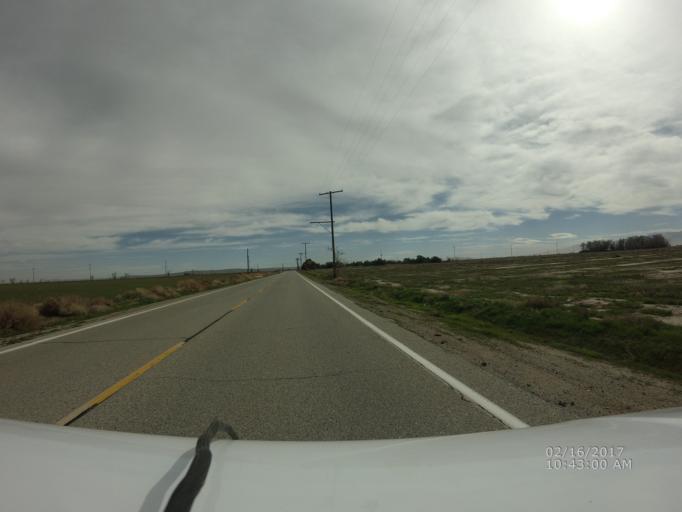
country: US
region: California
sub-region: Los Angeles County
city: Lancaster
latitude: 34.7197
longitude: -117.9731
